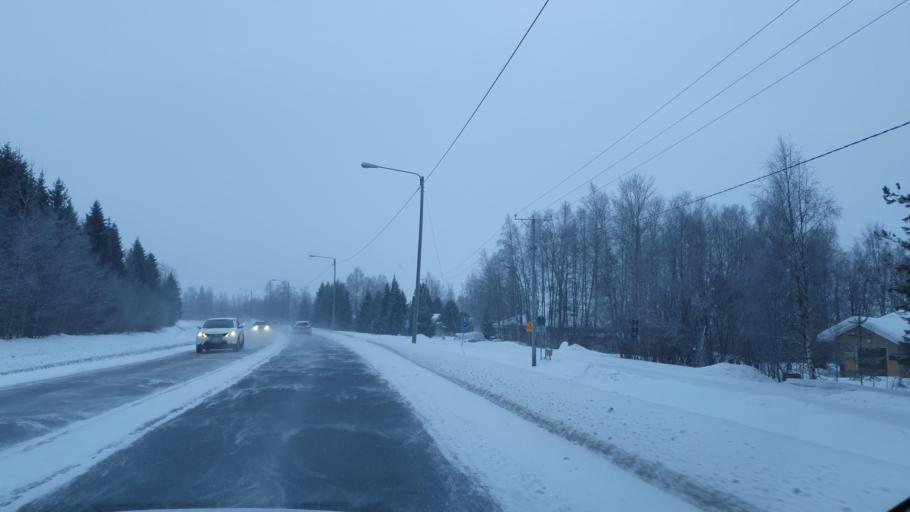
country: FI
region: Lapland
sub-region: Kemi-Tornio
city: Tornio
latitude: 65.8803
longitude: 24.1539
